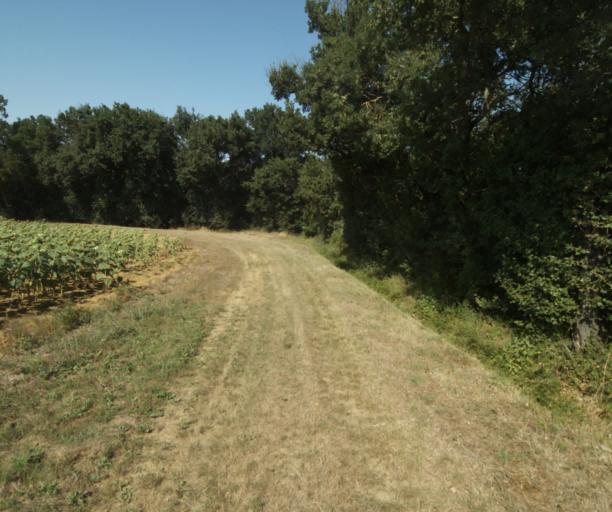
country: FR
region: Midi-Pyrenees
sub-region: Departement de la Haute-Garonne
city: Saint-Felix-Lauragais
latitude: 43.4410
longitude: 1.8424
